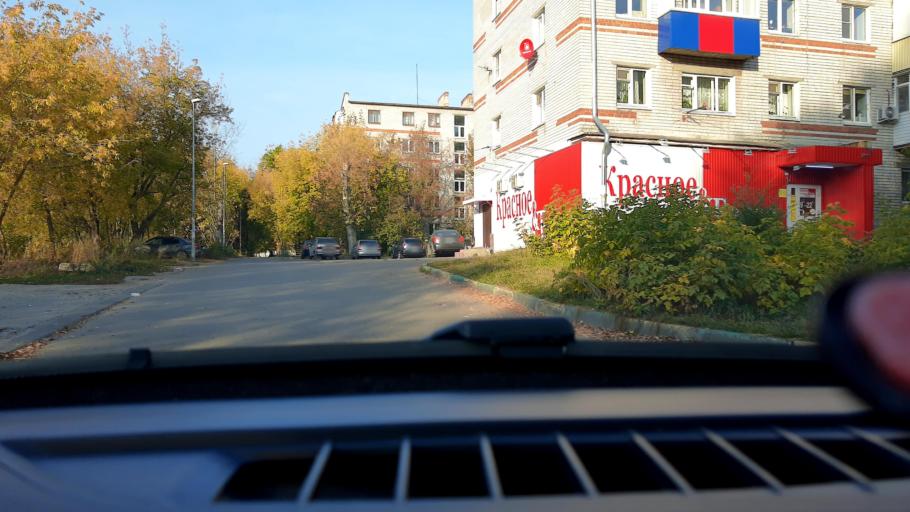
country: RU
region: Nizjnij Novgorod
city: Gorbatovka
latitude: 56.3398
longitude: 43.8291
